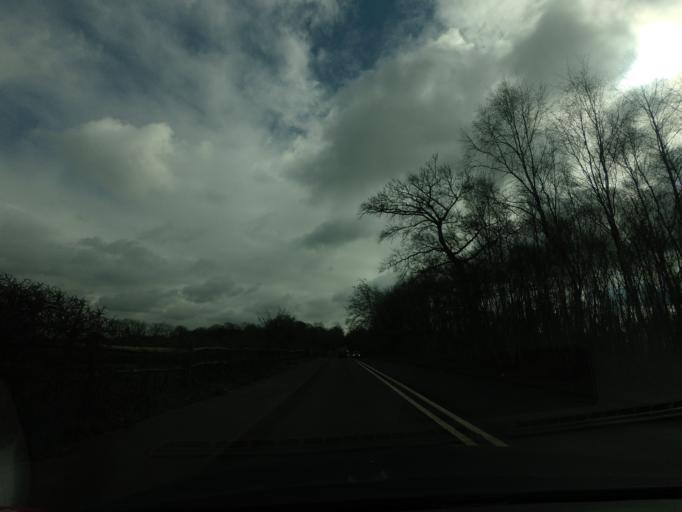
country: GB
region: England
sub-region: Kent
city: Kemsing
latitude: 51.2862
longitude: 0.2321
